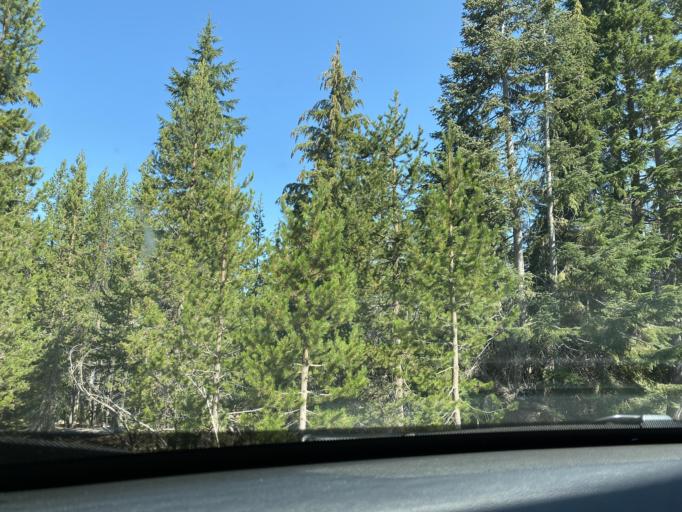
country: US
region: Oregon
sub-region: Deschutes County
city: Three Rivers
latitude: 43.7109
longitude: -121.2833
